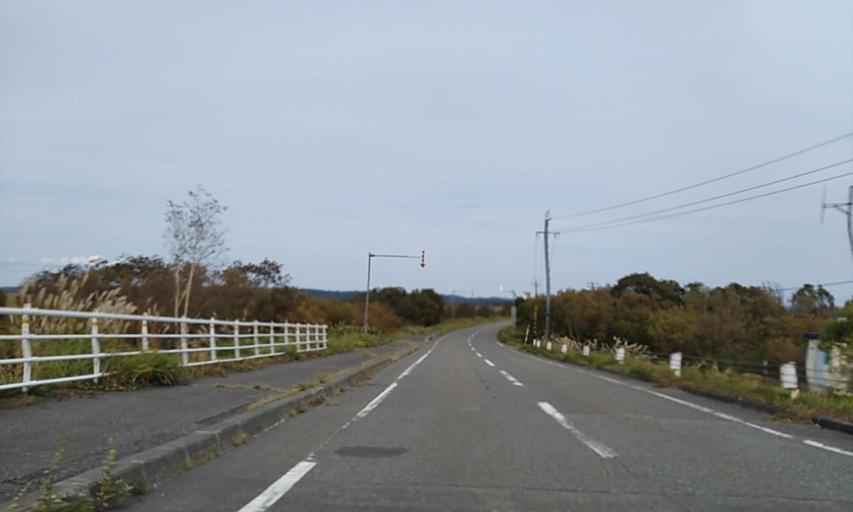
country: JP
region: Hokkaido
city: Makubetsu
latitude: 45.0043
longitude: 141.7097
